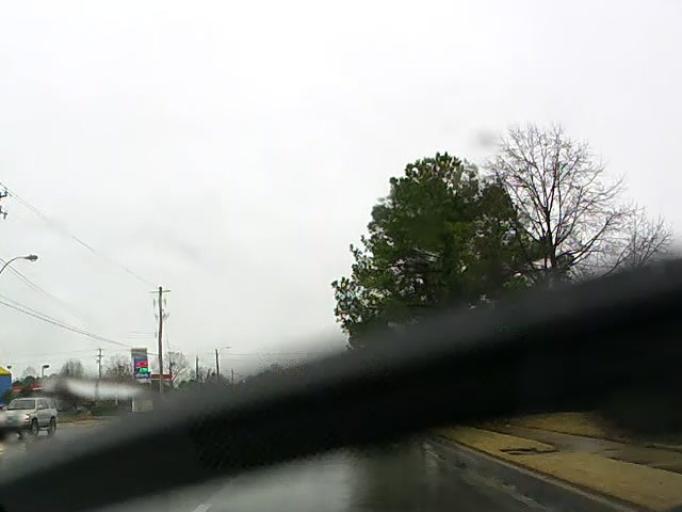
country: US
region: Tennessee
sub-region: Shelby County
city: Germantown
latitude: 35.0690
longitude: -89.8442
